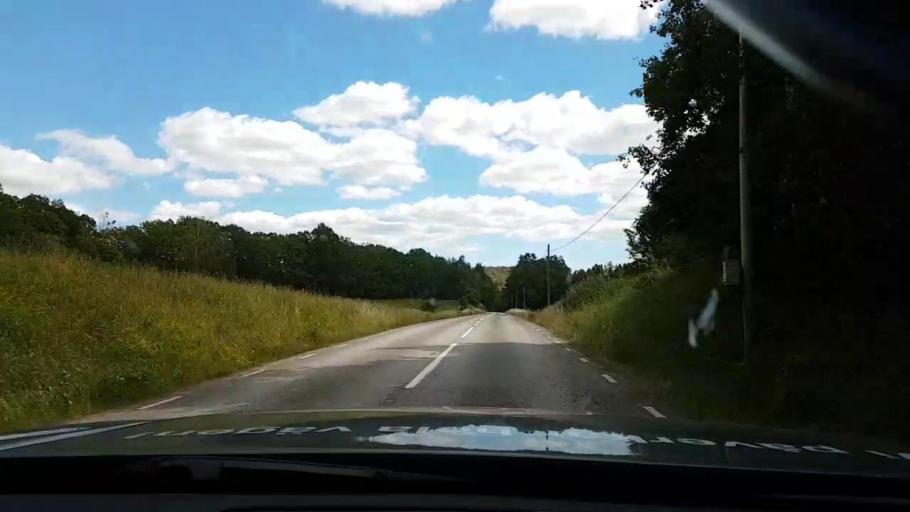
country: SE
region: Kalmar
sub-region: Vasterviks Kommun
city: Forserum
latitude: 58.0382
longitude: 16.4403
